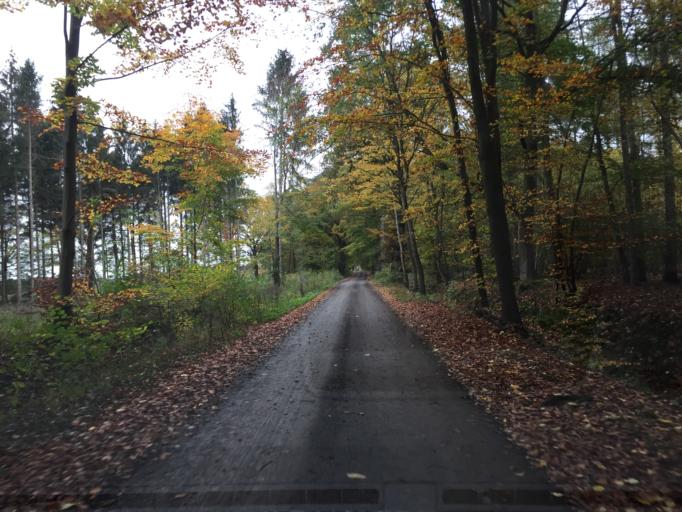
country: DE
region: Lower Saxony
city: Linsburg
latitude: 52.5823
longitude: 9.3135
